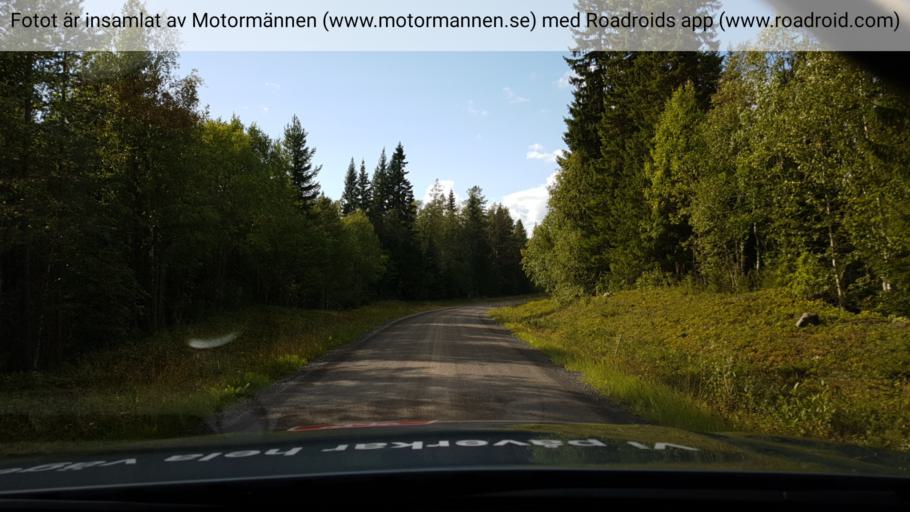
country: SE
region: Jaemtland
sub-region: OEstersunds Kommun
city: Lit
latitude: 63.3224
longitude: 15.2172
